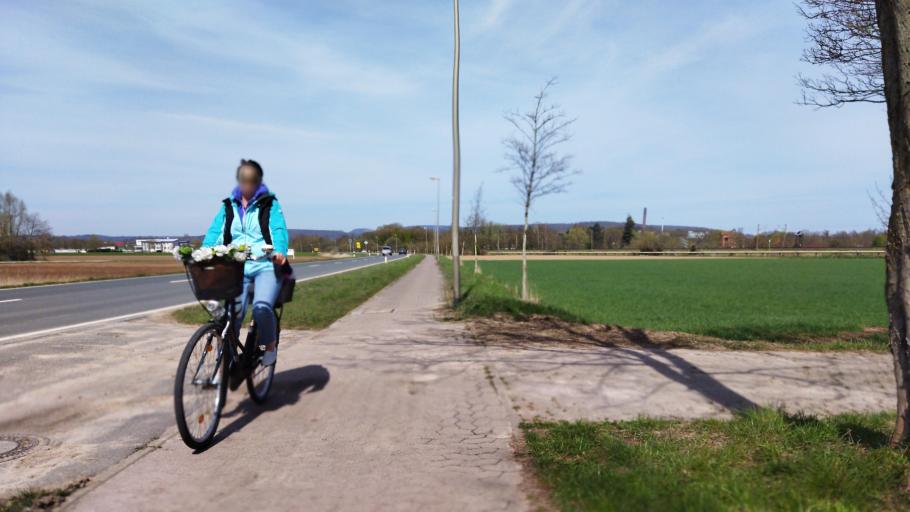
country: DE
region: Lower Saxony
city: Hameln
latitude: 52.0828
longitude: 9.3789
